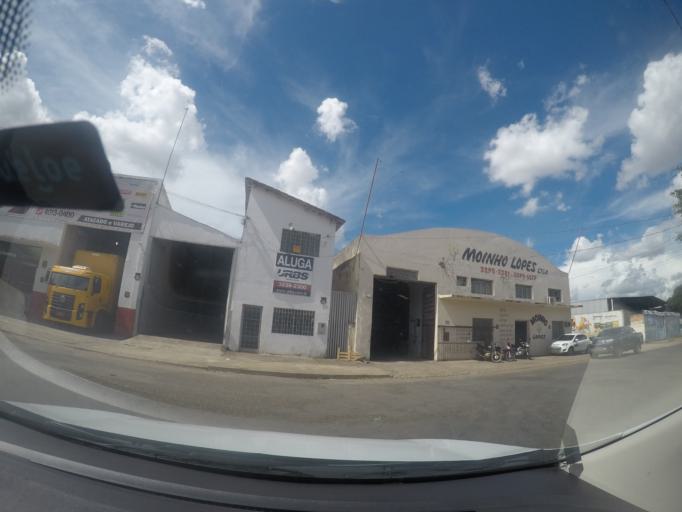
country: BR
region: Goias
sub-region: Goiania
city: Goiania
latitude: -16.6692
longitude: -49.3082
